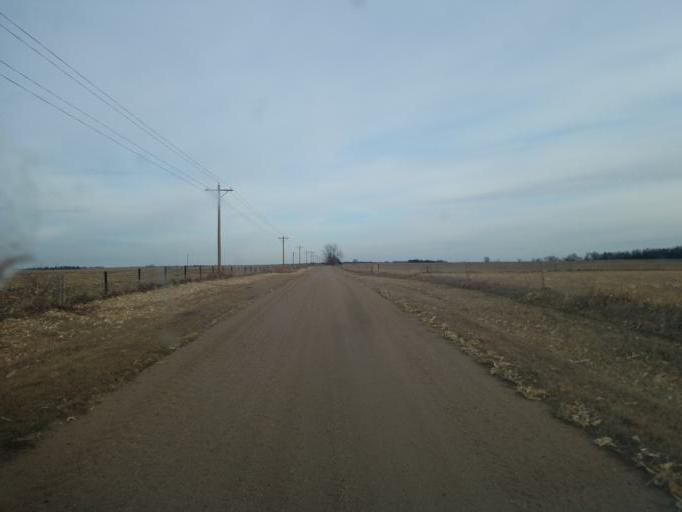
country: US
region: Nebraska
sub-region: Holt County
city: O'Neill
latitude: 42.4369
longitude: -98.3097
